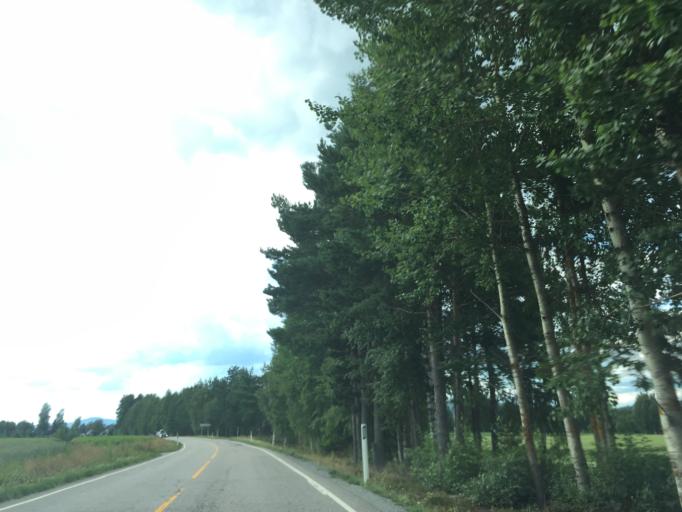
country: NO
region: Hedmark
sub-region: Kongsvinger
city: Spetalen
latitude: 60.2221
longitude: 11.8333
